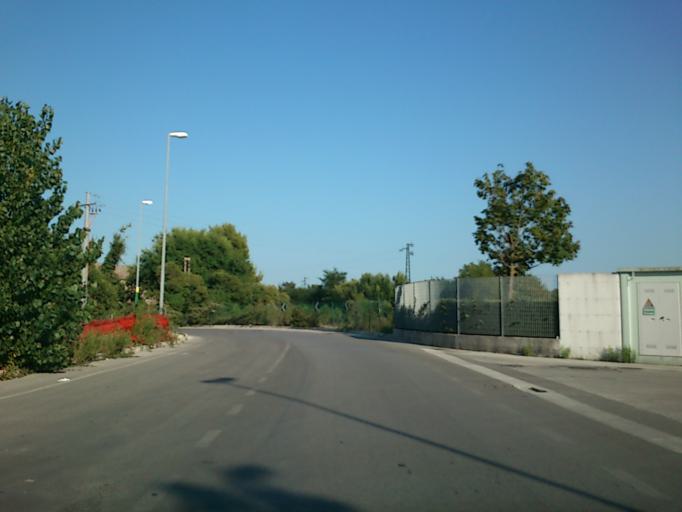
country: IT
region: The Marches
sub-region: Provincia di Pesaro e Urbino
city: Fano
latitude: 43.8263
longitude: 13.0444
